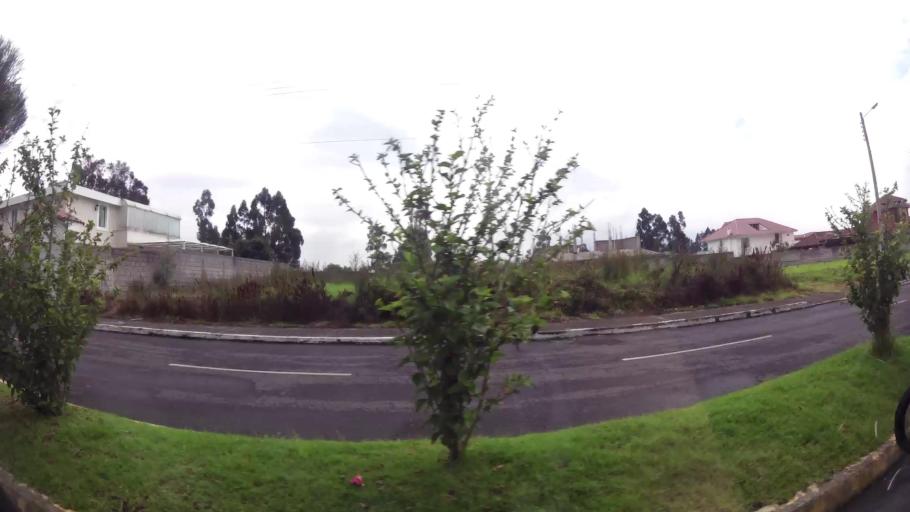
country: EC
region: Pichincha
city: Sangolqui
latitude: -0.3088
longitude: -78.4752
